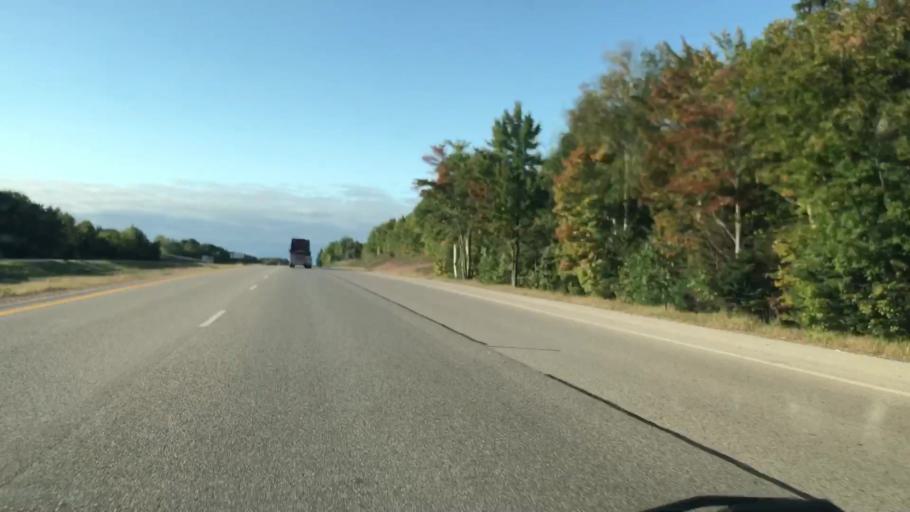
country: US
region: Michigan
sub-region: Chippewa County
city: Sault Ste. Marie
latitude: 46.4593
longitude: -84.3834
